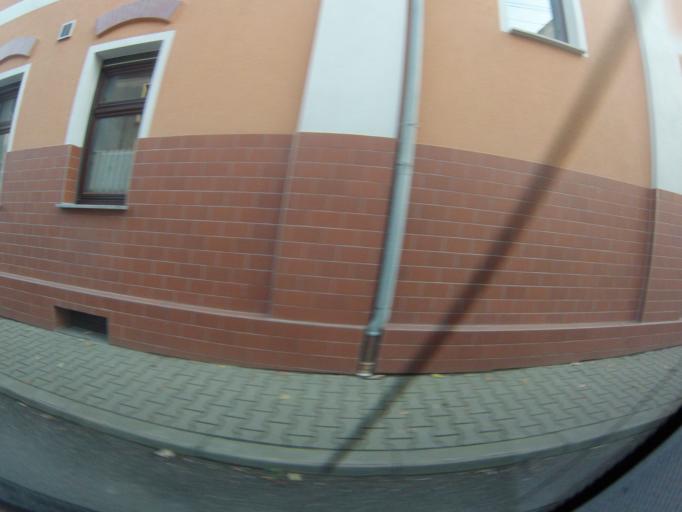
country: DE
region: Thuringia
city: Gossnitz
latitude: 50.8928
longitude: 12.3990
